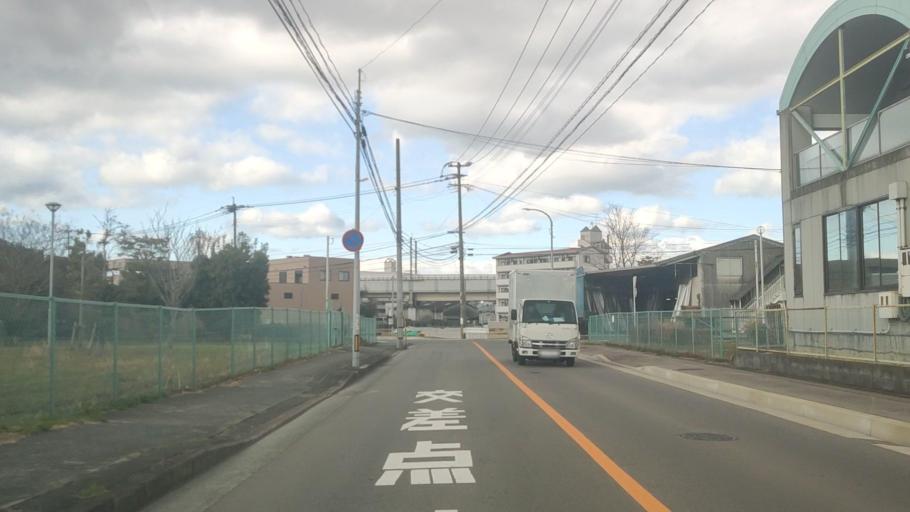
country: JP
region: Fukuoka
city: Fukuoka-shi
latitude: 33.6117
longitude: 130.4328
